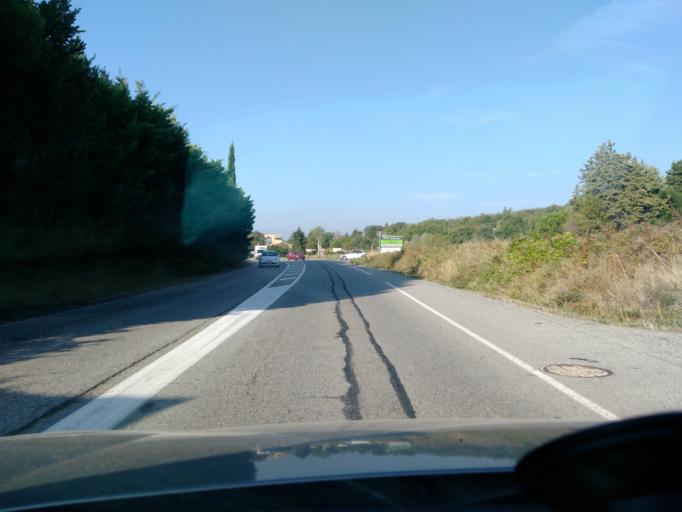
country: FR
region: Rhone-Alpes
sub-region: Departement de la Drome
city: La Garde-Adhemar
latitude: 44.4200
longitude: 4.8118
